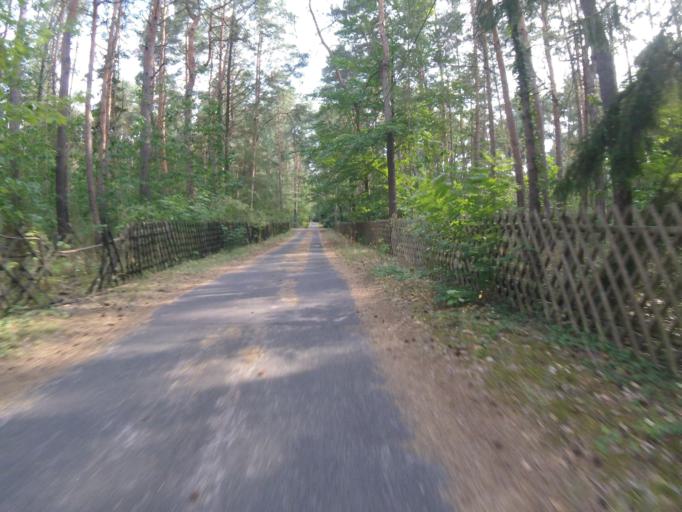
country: DE
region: Brandenburg
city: Munchehofe
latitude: 52.2470
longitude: 13.7779
